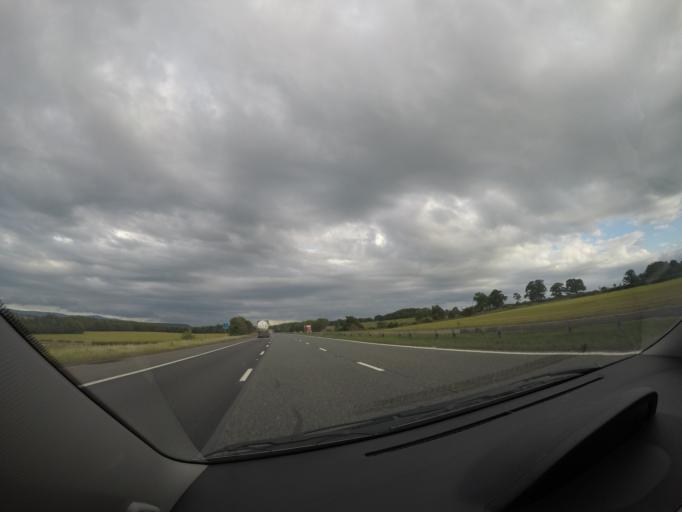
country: GB
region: England
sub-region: Cumbria
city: Scotby
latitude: 54.7679
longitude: -2.8407
